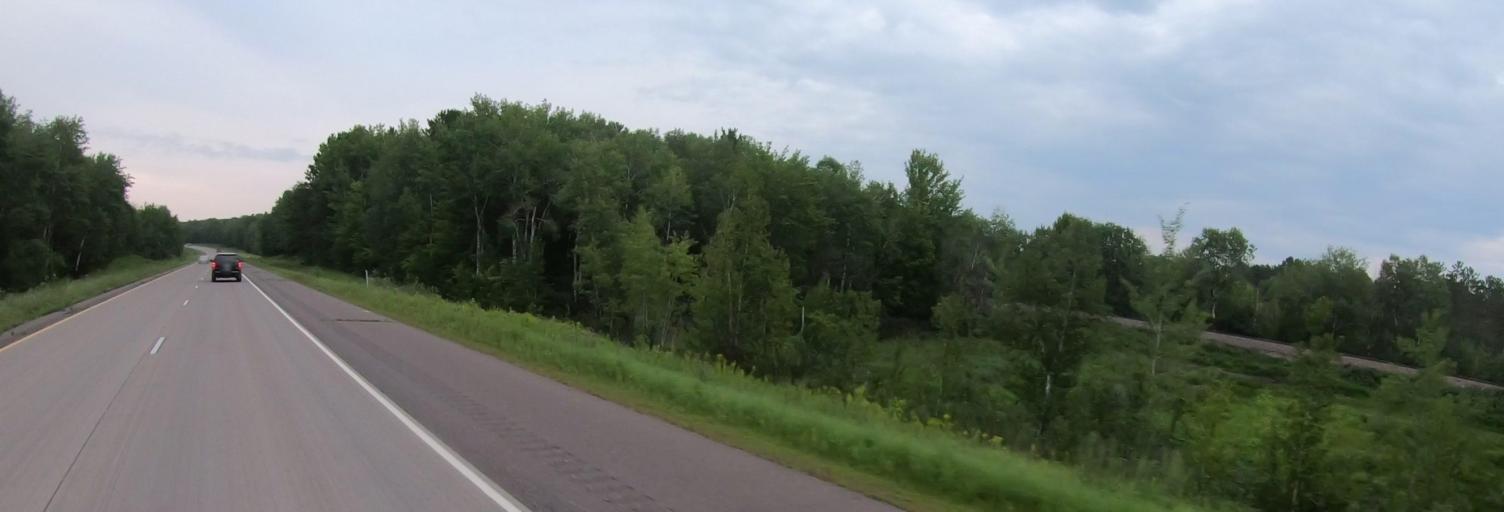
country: US
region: Minnesota
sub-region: Pine County
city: Sandstone
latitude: 46.0971
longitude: -92.8904
